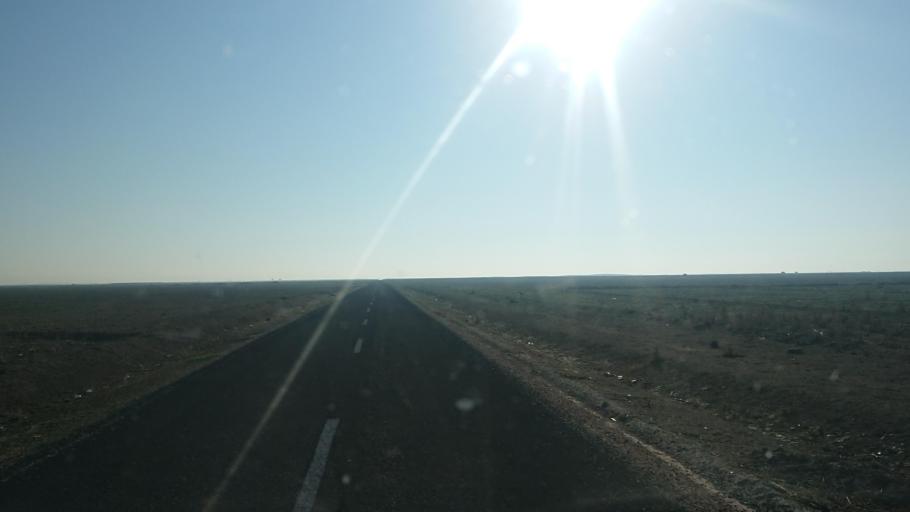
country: TR
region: Aksaray
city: Yesilova
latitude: 38.3880
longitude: 33.7511
